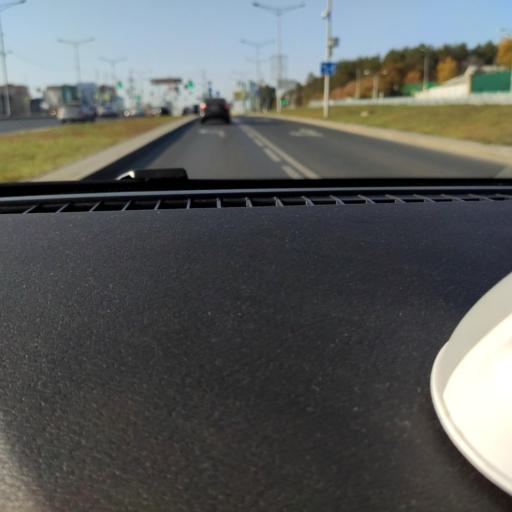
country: RU
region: Samara
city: Samara
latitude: 53.2646
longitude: 50.2452
